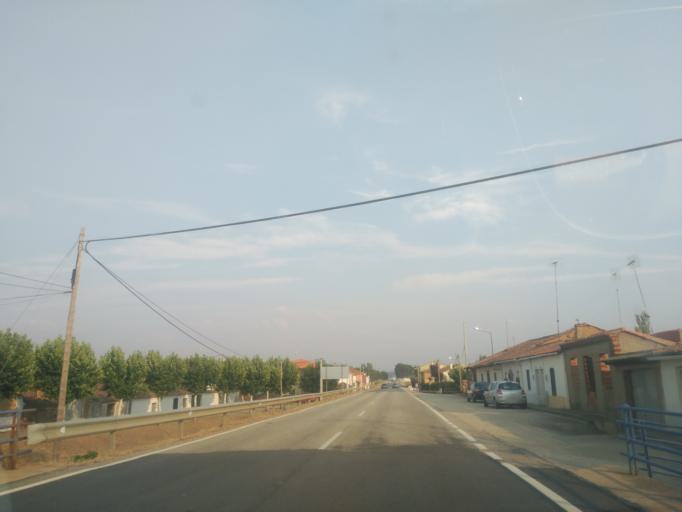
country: ES
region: Castille and Leon
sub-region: Provincia de Zamora
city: Pozuelo de Tabara
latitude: 41.7849
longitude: -5.8952
